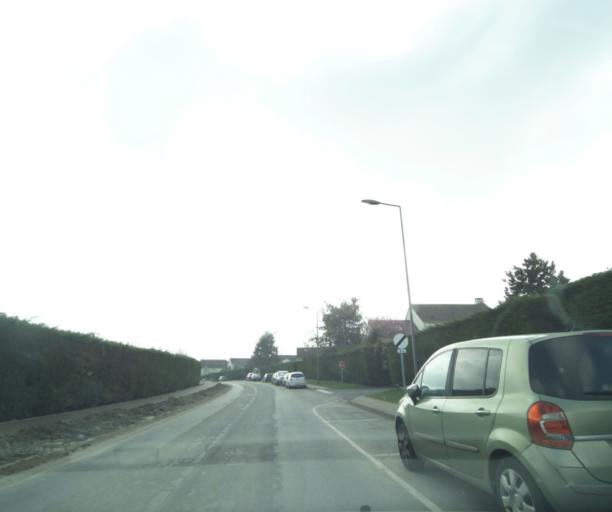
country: FR
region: Ile-de-France
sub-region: Departement du Val-d'Oise
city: Vaureal
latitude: 49.0421
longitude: 2.0199
